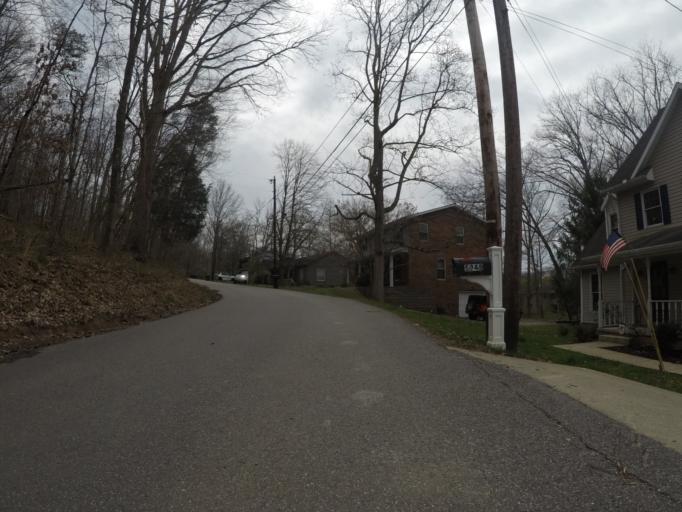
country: US
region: West Virginia
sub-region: Cabell County
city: Pea Ridge
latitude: 38.4195
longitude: -82.3247
